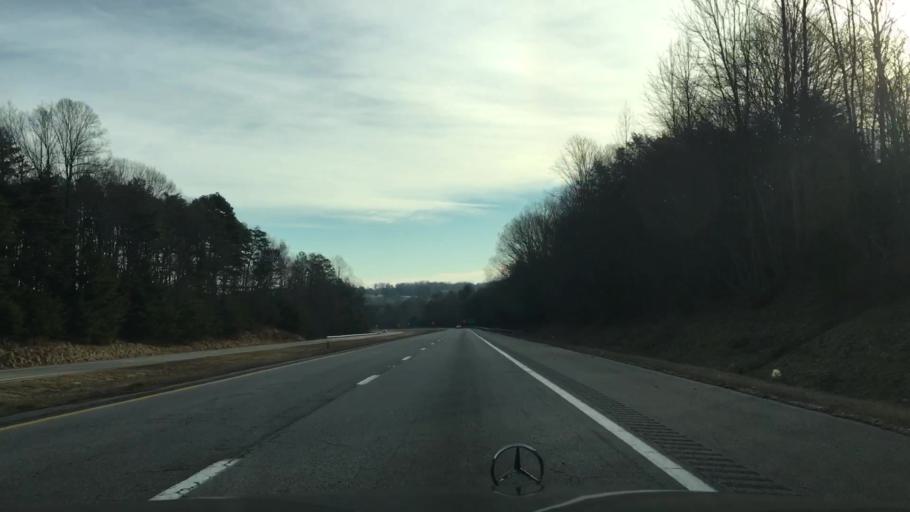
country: US
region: Virginia
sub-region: City of Danville
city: Danville
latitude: 36.5454
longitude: -79.4217
